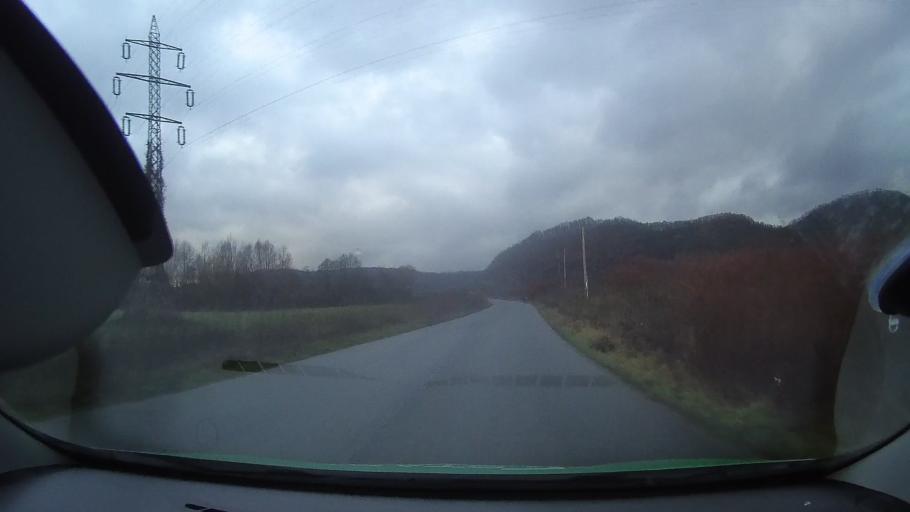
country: RO
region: Hunedoara
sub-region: Comuna Baia de Cris
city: Baia de Cris
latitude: 46.1827
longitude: 22.7163
